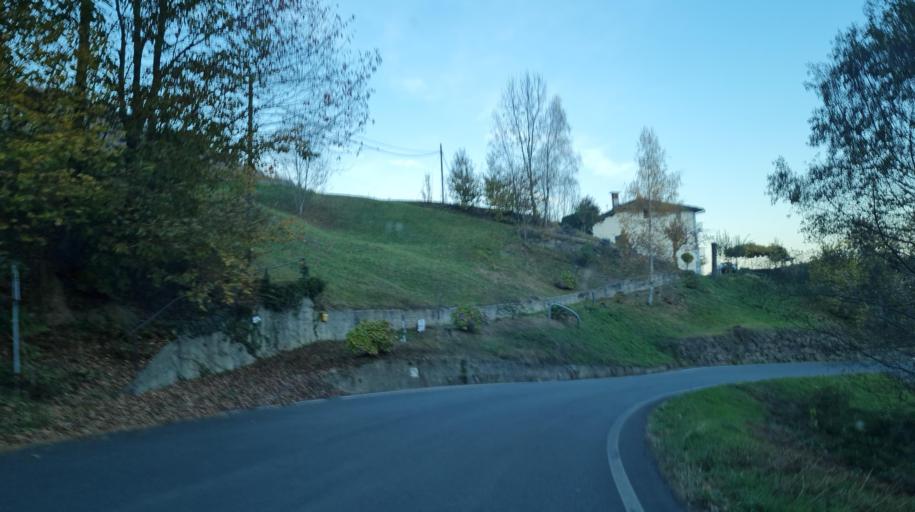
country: IT
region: Piedmont
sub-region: Provincia di Torino
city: Trausella
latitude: 45.5005
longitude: 7.7593
